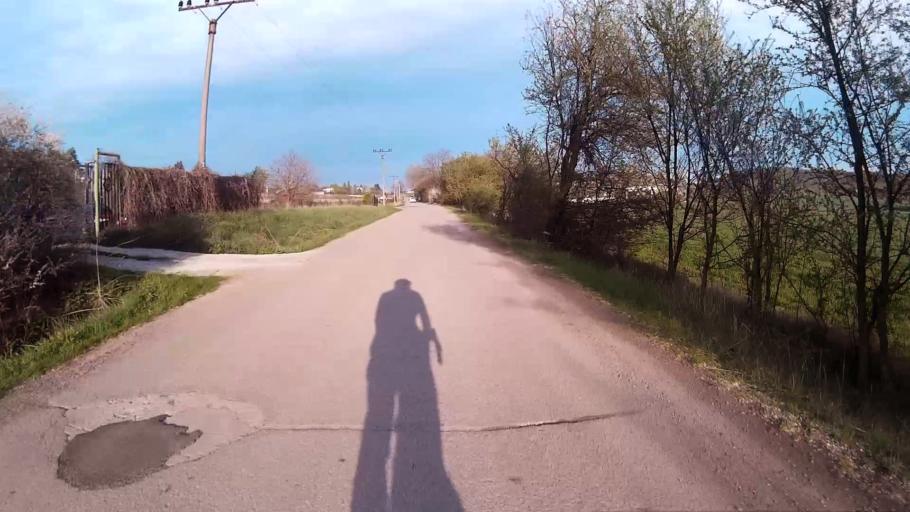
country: CZ
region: South Moravian
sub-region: Mesto Brno
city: Mokra Hora
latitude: 49.2421
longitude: 16.5566
